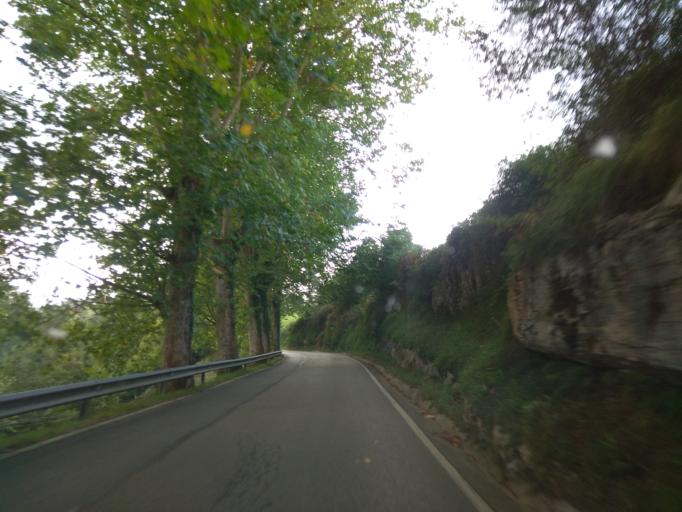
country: ES
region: Cantabria
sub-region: Provincia de Cantabria
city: San Vicente de la Barquera
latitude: 43.3248
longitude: -4.3564
